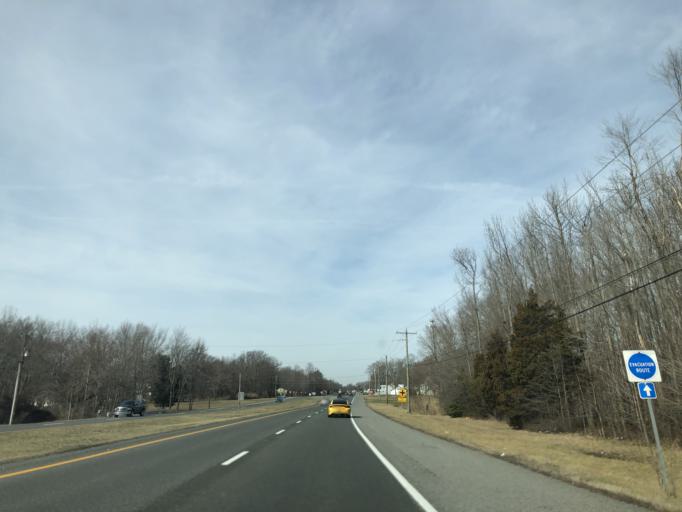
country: US
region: Delaware
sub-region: Kent County
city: Clayton
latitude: 39.3482
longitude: -75.6401
